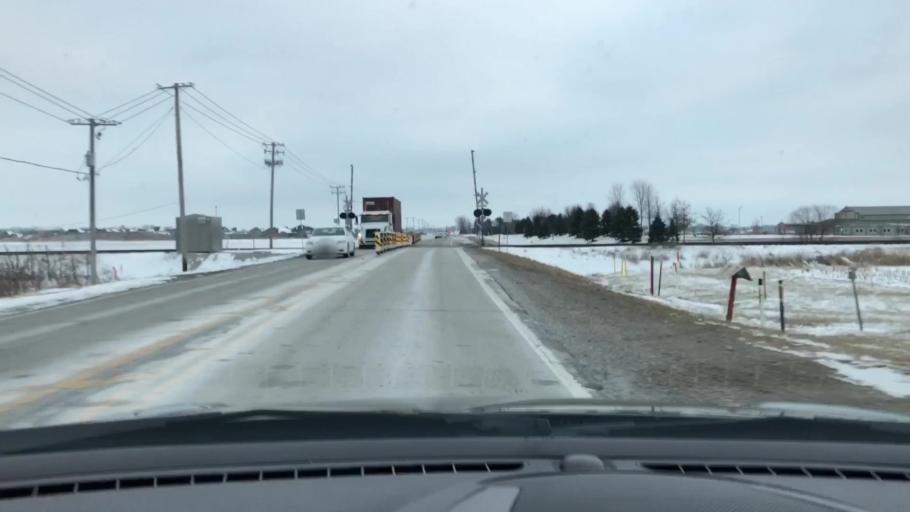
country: US
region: Illinois
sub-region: Will County
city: New Lenox
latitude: 41.4923
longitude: -88.0037
